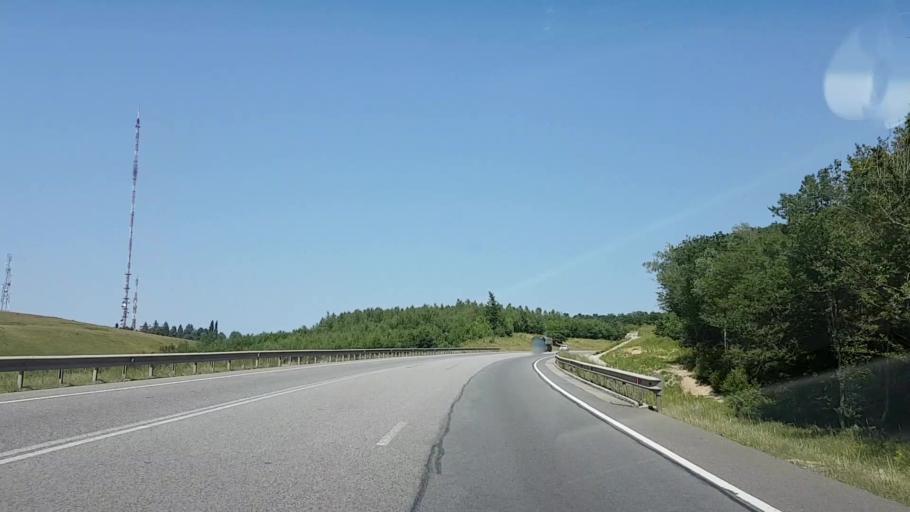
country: RO
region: Cluj
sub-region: Comuna Feleacu
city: Feleacu
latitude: 46.7064
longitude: 23.6428
